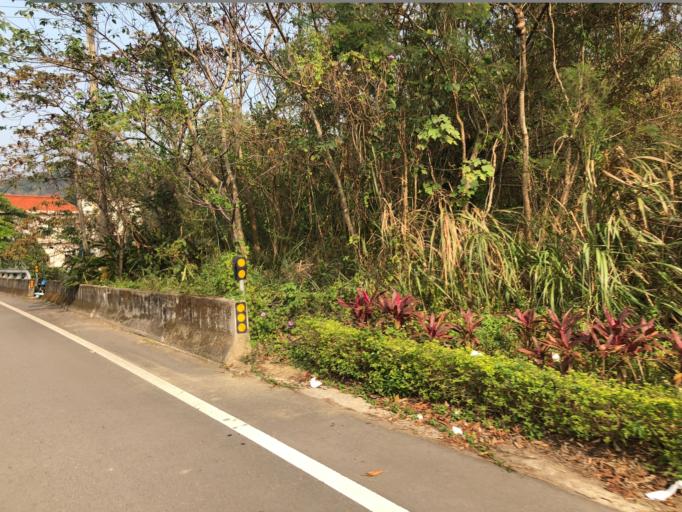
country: TW
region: Taiwan
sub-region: Miaoli
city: Miaoli
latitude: 24.6097
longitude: 120.9589
